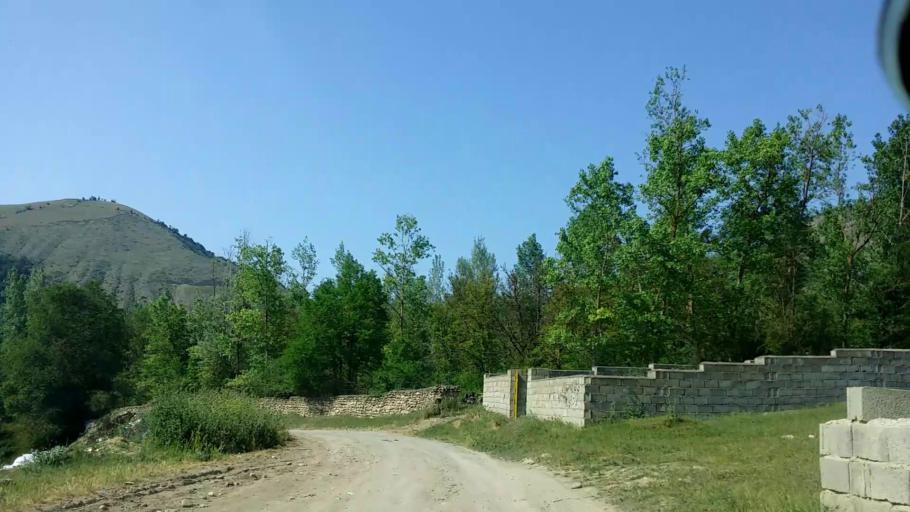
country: IR
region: Mazandaran
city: `Abbasabad
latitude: 36.5365
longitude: 51.2140
